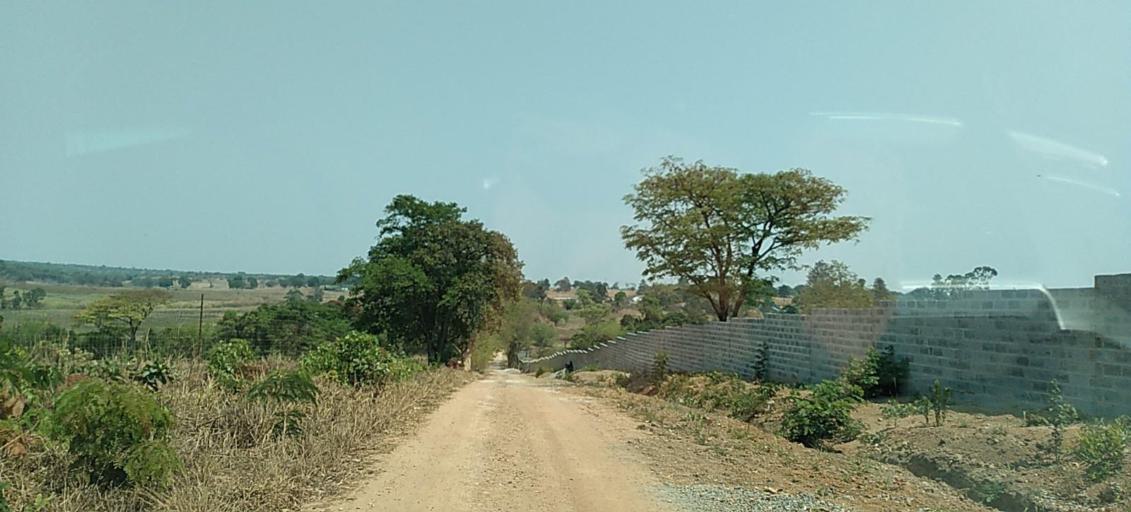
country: ZM
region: Copperbelt
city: Chambishi
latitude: -12.6306
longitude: 27.9433
